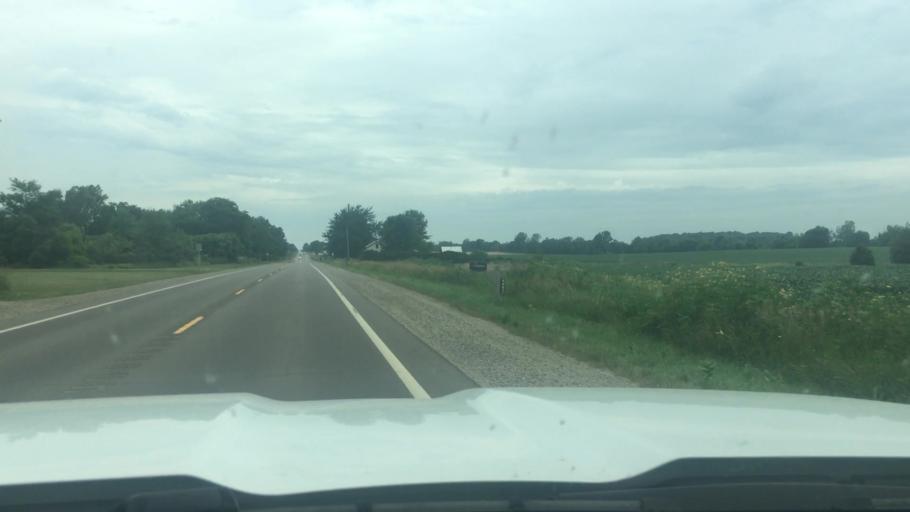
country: US
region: Michigan
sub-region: Clinton County
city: Saint Johns
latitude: 43.0015
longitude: -84.6111
